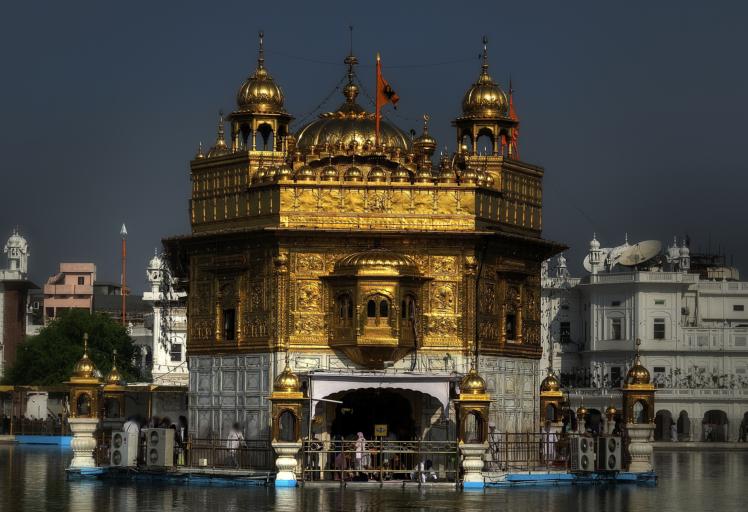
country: IN
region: Punjab
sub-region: Amritsar
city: Amritsar
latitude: 31.6195
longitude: 74.8772
